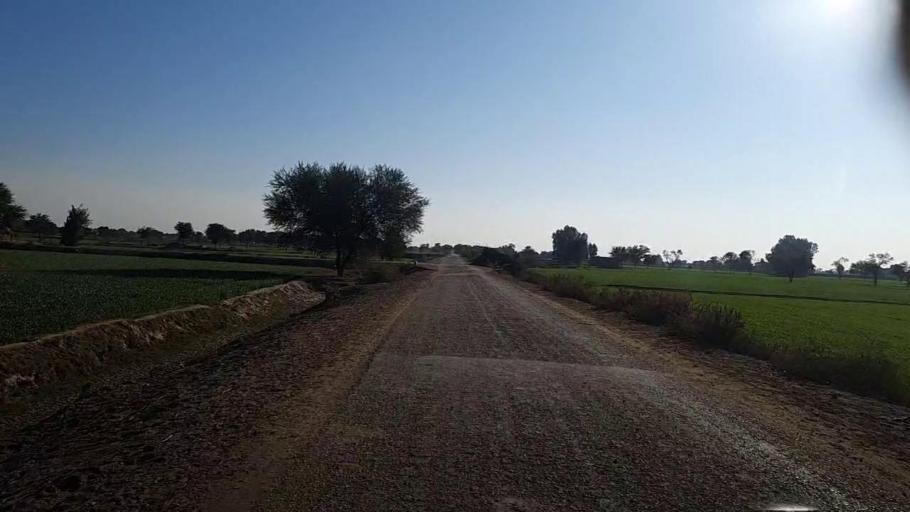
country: PK
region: Sindh
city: Khairpur
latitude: 27.8930
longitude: 69.7462
